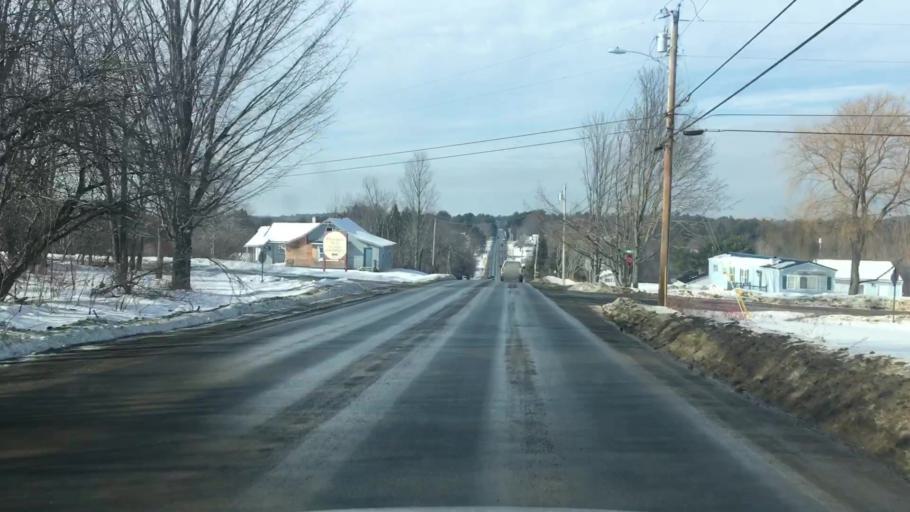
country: US
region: Maine
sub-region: Penobscot County
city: Hermon
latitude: 44.8488
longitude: -68.8754
